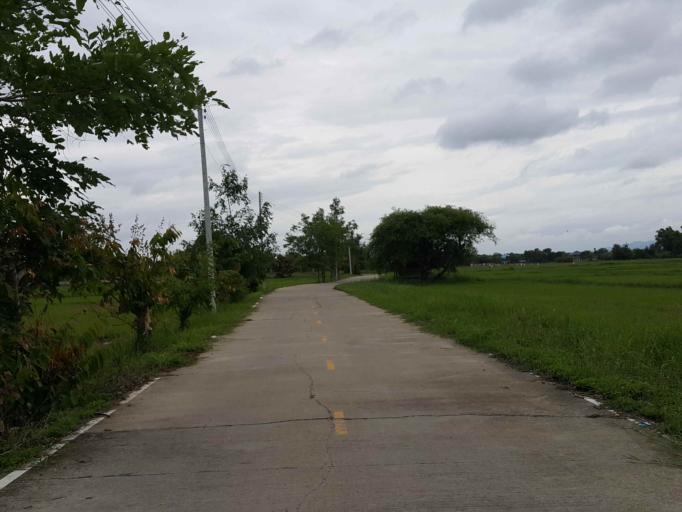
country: TH
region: Chiang Mai
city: San Sai
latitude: 18.8208
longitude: 99.0737
